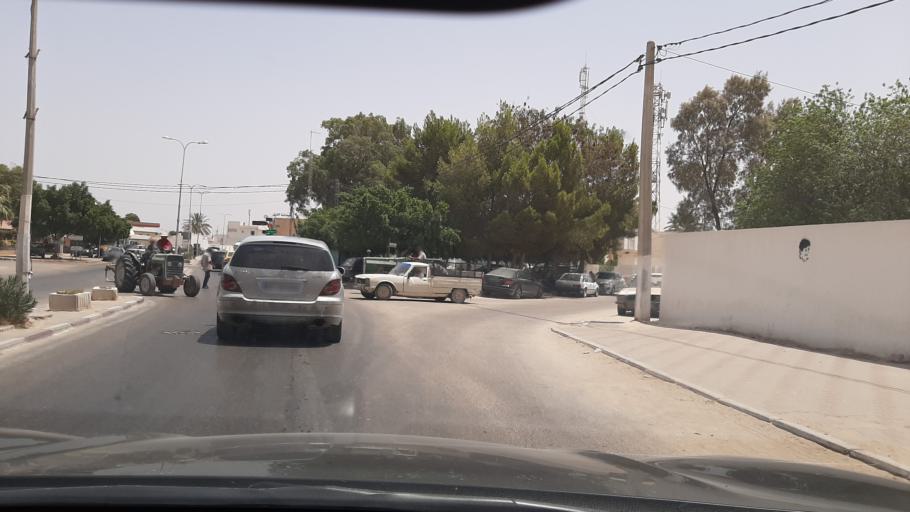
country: TN
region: Qabis
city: Matmata
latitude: 33.6176
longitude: 10.2861
